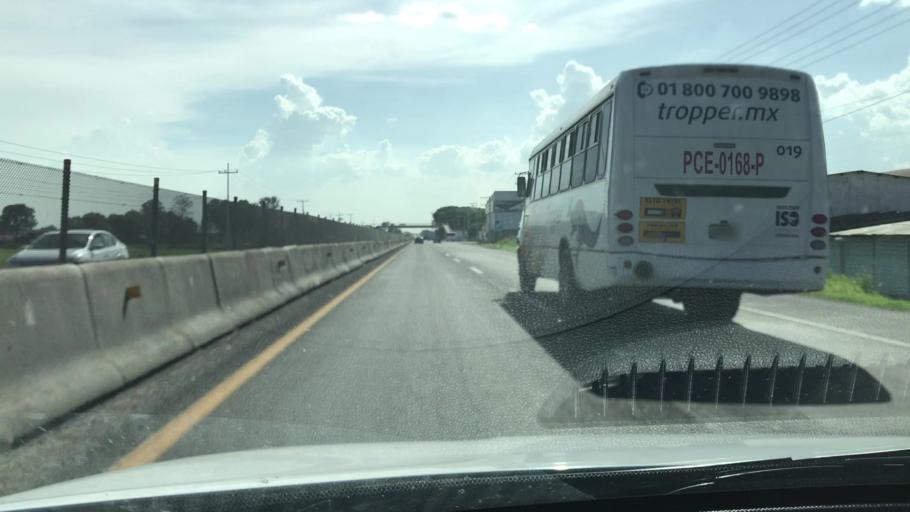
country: MX
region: Guanajuato
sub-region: Villagran
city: El Chinaco (El Pujido)
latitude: 20.5138
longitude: -100.9181
